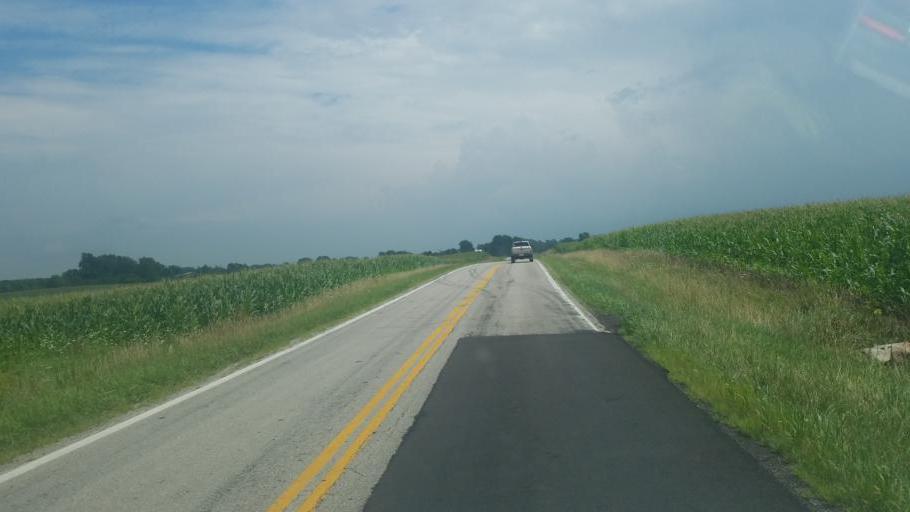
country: US
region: Ohio
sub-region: Champaign County
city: North Lewisburg
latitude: 40.4009
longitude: -83.5293
